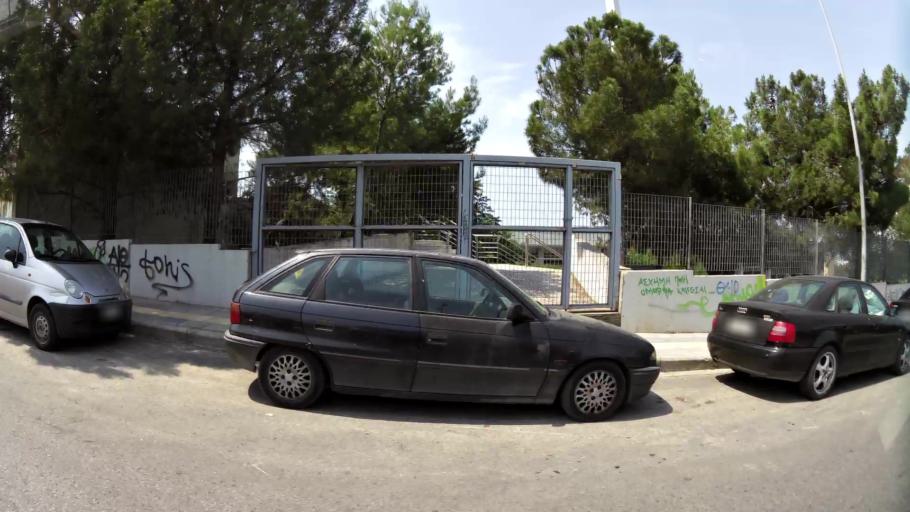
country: GR
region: Central Macedonia
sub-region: Nomos Thessalonikis
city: Triandria
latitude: 40.6267
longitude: 22.9677
